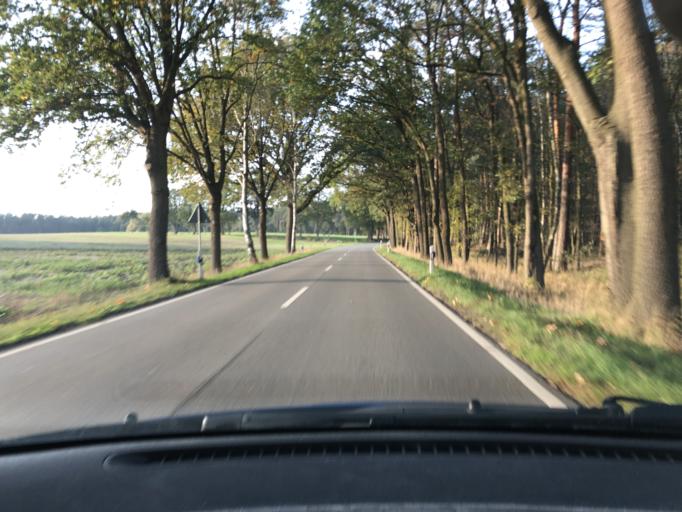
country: DE
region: Lower Saxony
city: Hitzacker
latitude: 53.1206
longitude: 11.0518
